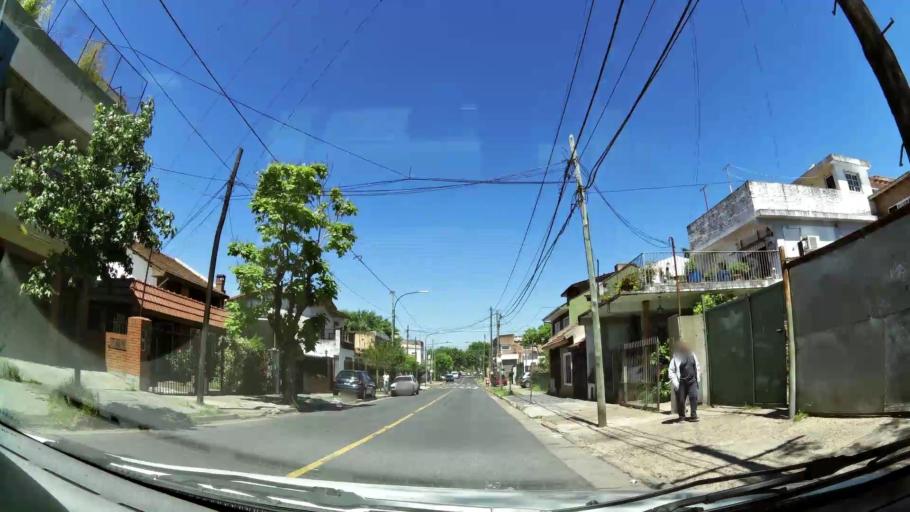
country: AR
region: Buenos Aires
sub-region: Partido de San Isidro
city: San Isidro
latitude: -34.5078
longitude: -58.5536
